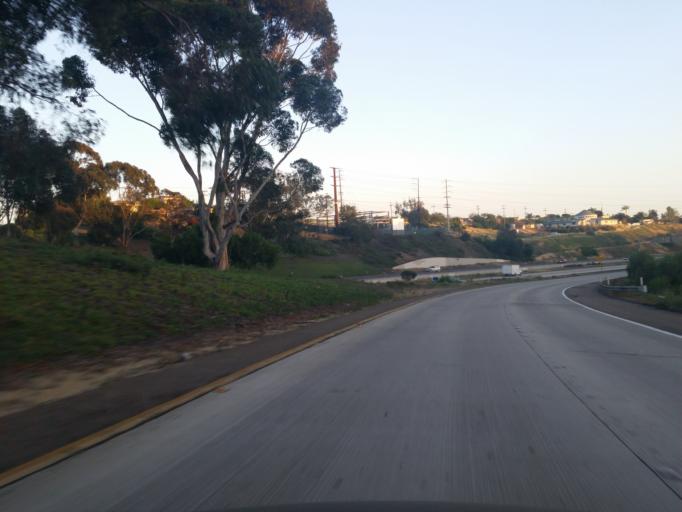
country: US
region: California
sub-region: San Diego County
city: San Diego
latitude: 32.7321
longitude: -117.1125
